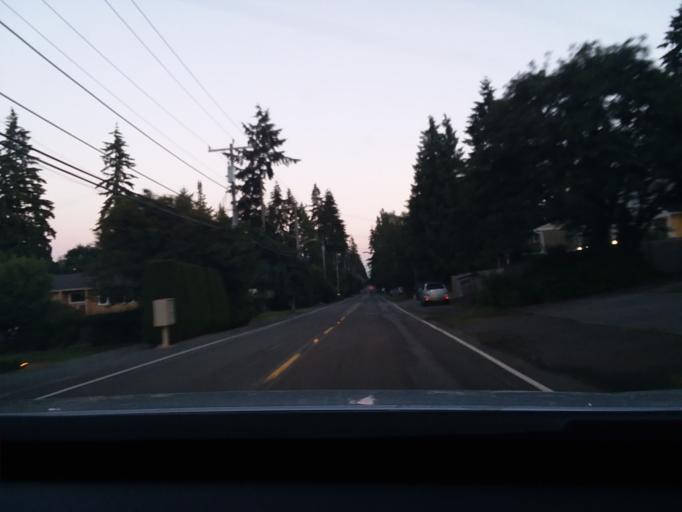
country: US
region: Washington
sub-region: King County
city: Shoreline
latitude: 47.7592
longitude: -122.3404
